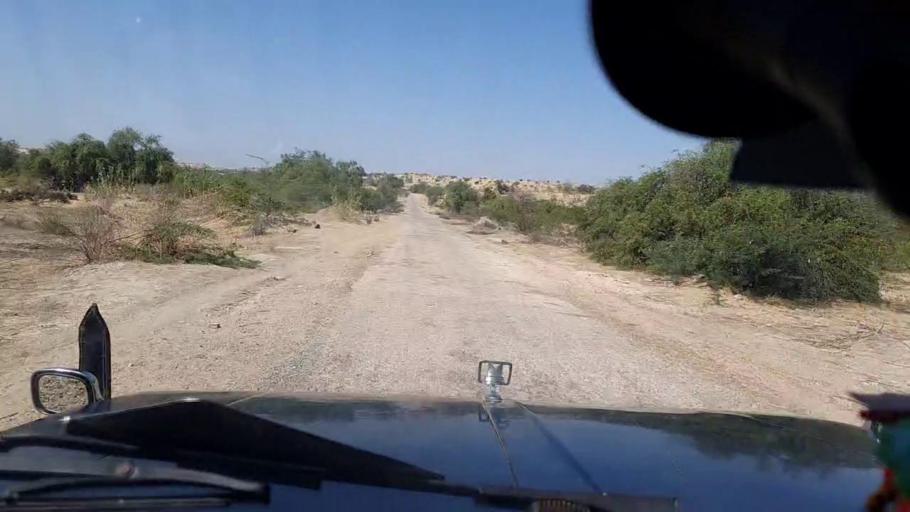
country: PK
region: Sindh
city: Mithi
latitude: 24.6136
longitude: 69.6959
